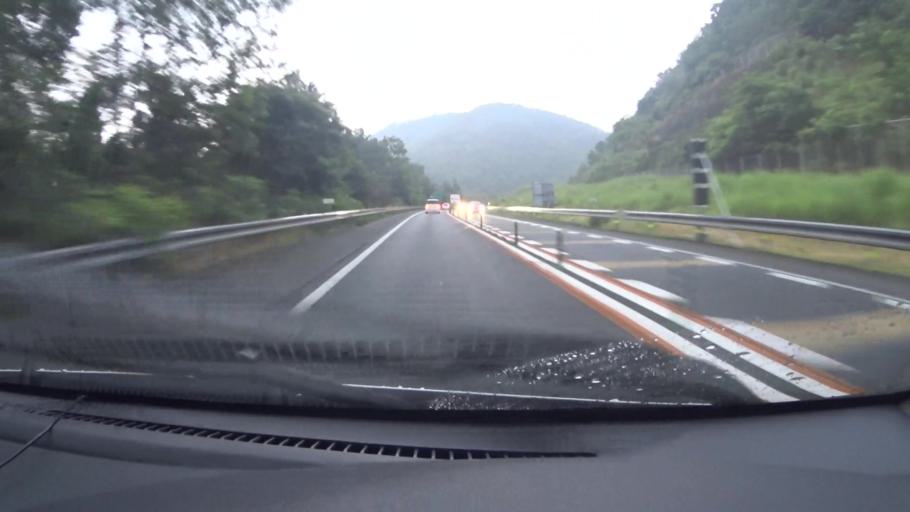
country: JP
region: Kyoto
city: Kameoka
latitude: 35.1443
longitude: 135.4386
